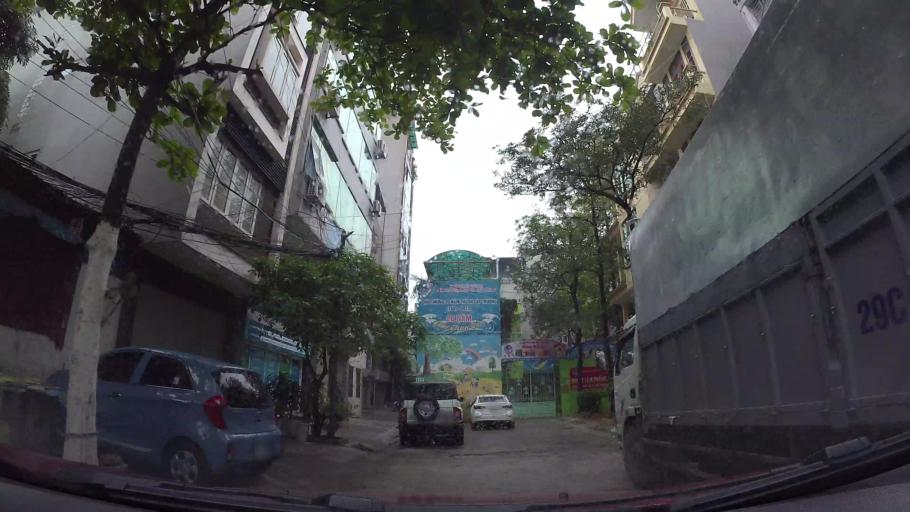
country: VN
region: Ha Noi
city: Dong Da
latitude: 21.0154
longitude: 105.8260
